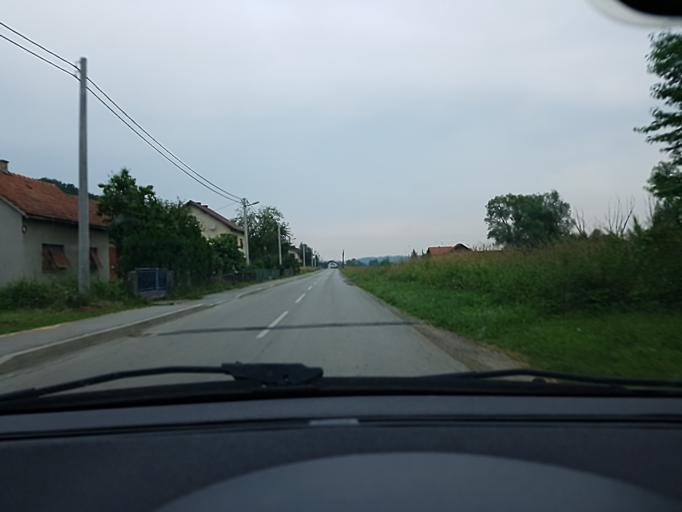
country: HR
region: Zagrebacka
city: Jakovlje
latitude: 45.9866
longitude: 15.8412
